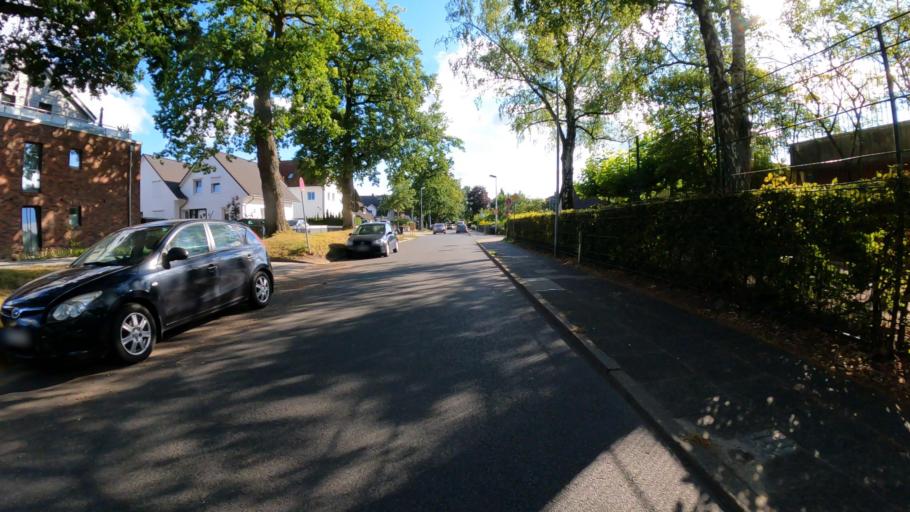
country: DE
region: Schleswig-Holstein
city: Ahrensburg
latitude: 53.6418
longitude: 10.2173
